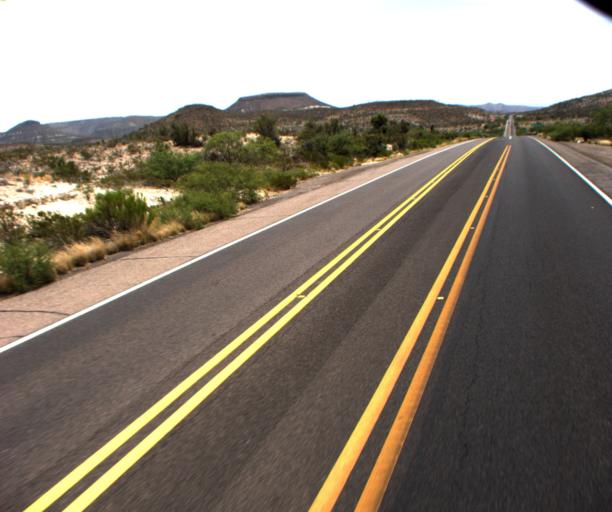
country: US
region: Arizona
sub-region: Gila County
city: Peridot
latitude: 33.2864
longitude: -110.3739
